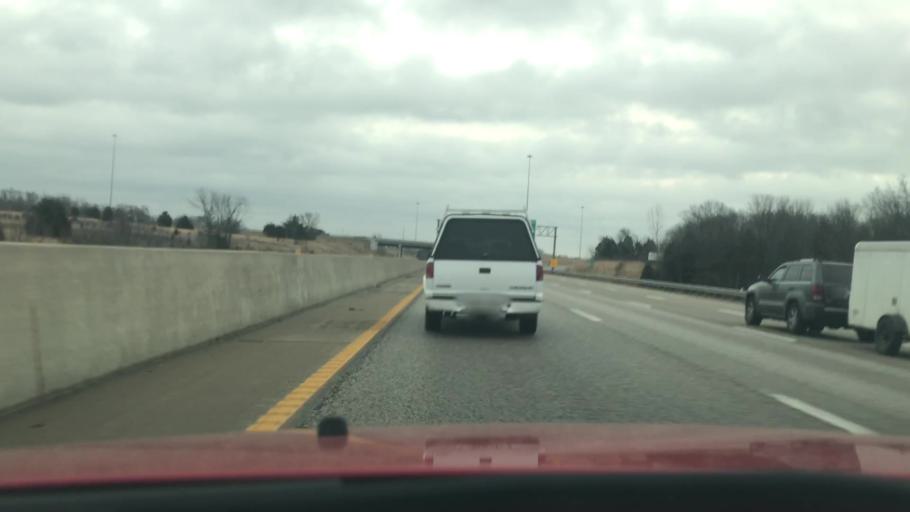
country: US
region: Missouri
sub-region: Saint Charles County
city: Wentzville
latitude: 38.8061
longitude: -90.8439
